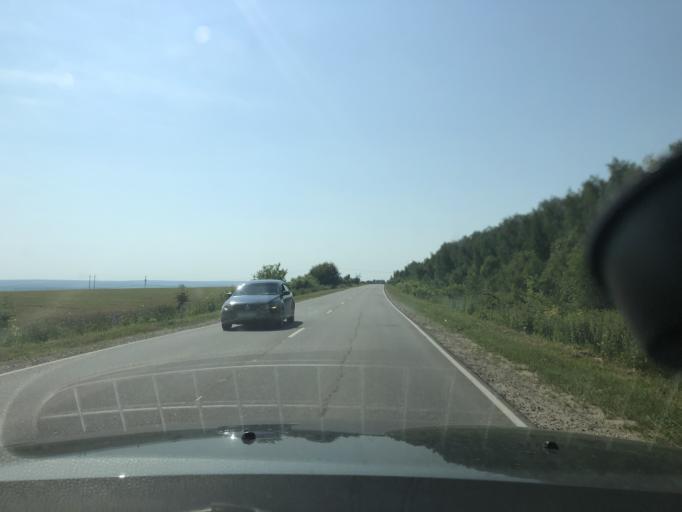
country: RU
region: Tula
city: Dubna
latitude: 54.1217
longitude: 37.0750
